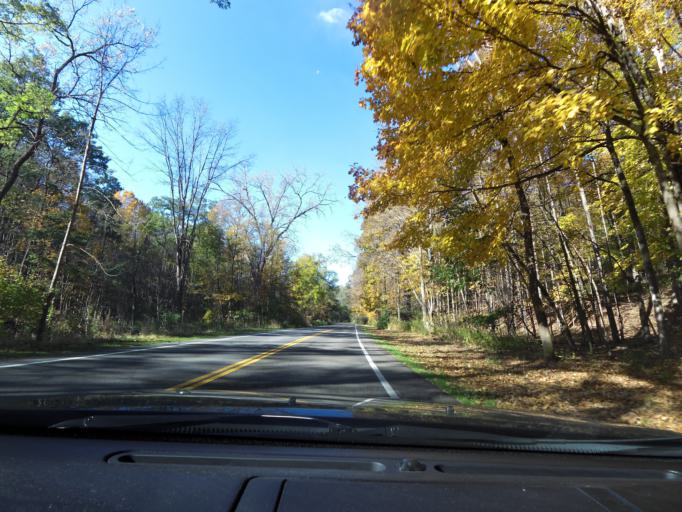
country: US
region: New York
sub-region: Wyoming County
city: Perry
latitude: 42.6975
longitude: -77.9478
